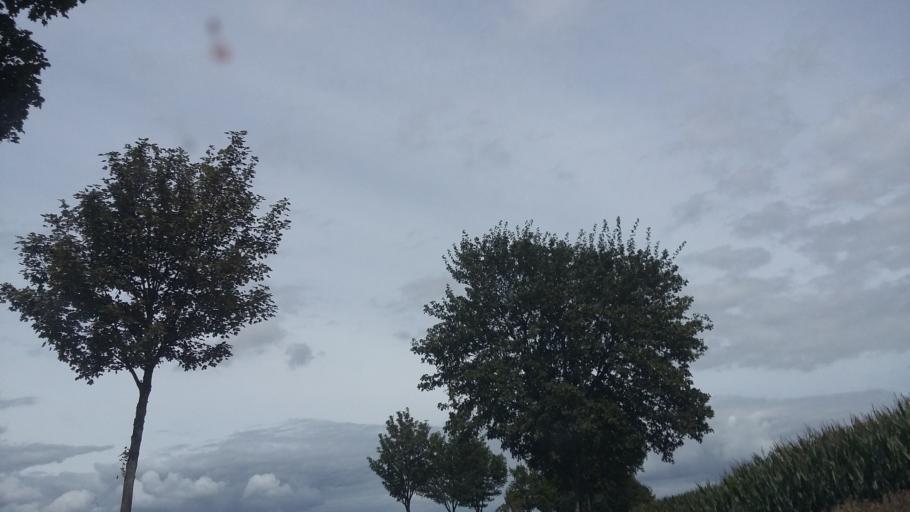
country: DE
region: Lower Saxony
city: Harsum
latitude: 52.1944
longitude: 10.0071
